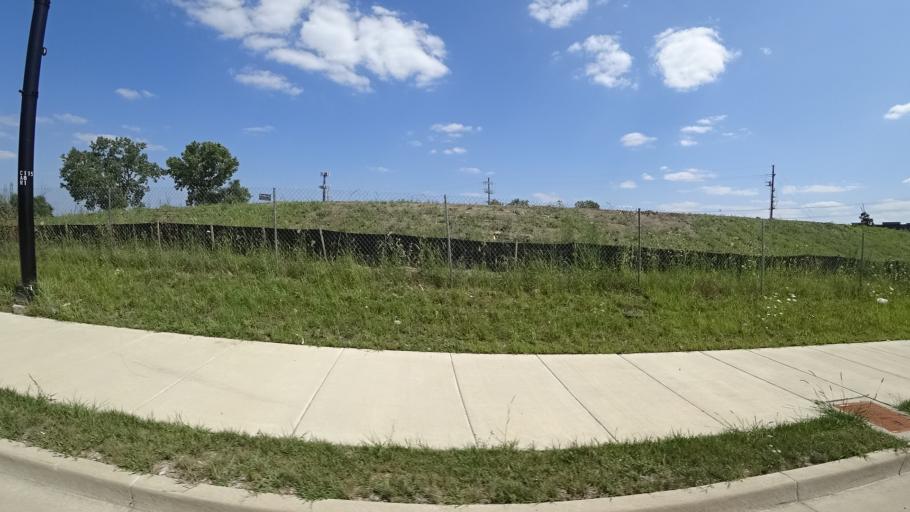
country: US
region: Illinois
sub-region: Cook County
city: Orland Park
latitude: 41.6376
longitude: -87.8537
